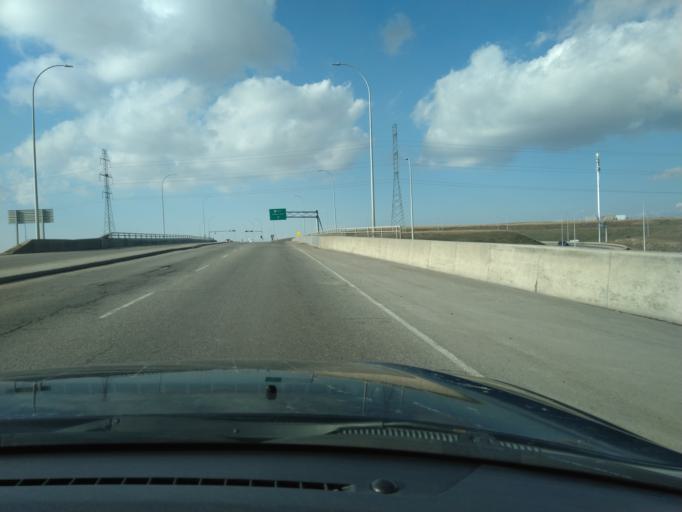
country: CA
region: Alberta
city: Calgary
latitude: 51.1725
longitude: -114.0688
